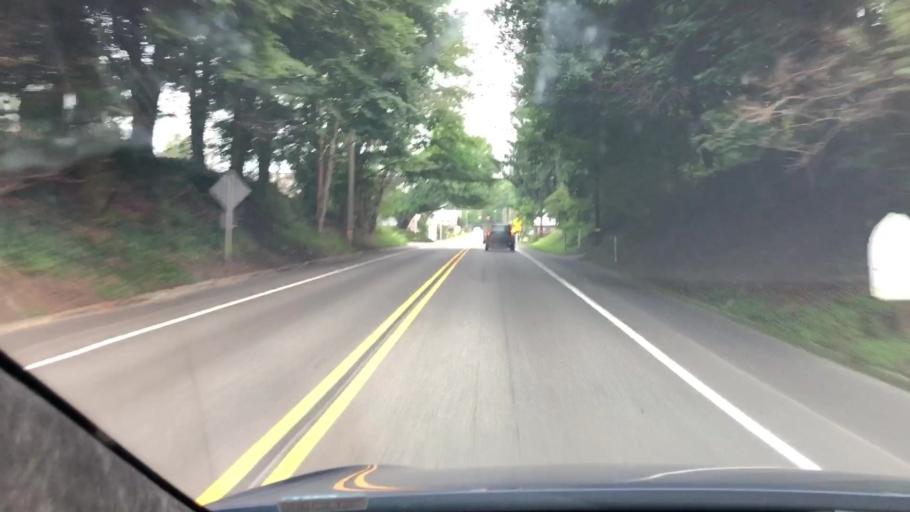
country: US
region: Pennsylvania
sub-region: Butler County
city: Slippery Rock
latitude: 41.1086
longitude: -80.0062
